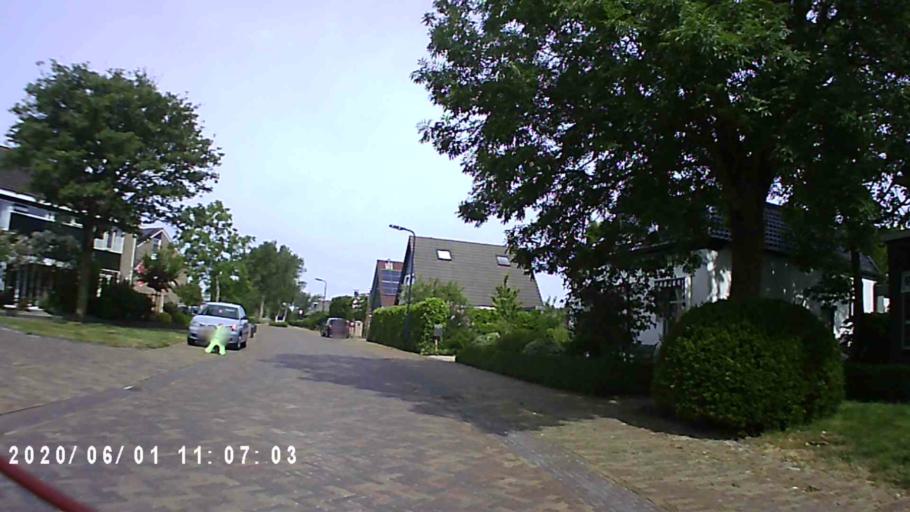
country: NL
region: Friesland
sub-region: Gemeente Franekeradeel
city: Sexbierum
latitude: 53.1966
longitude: 5.4597
